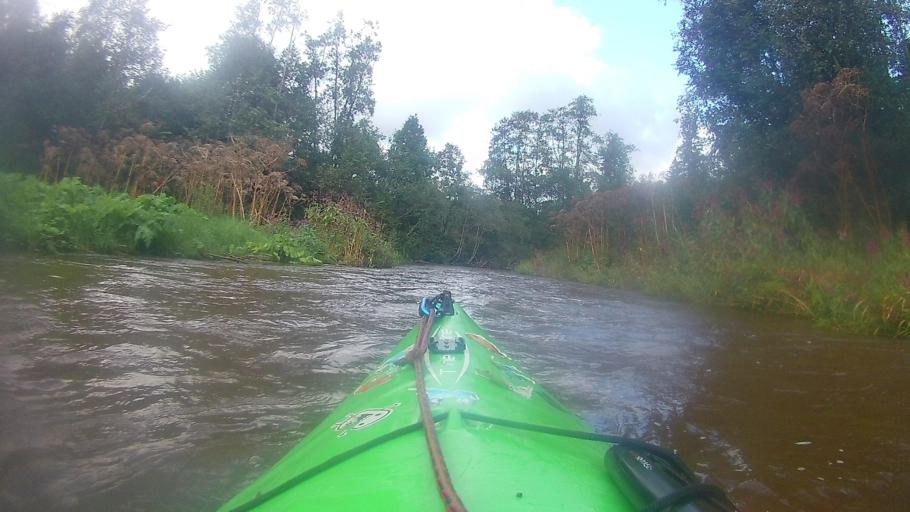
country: LV
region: Talsu Rajons
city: Sabile
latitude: 56.9989
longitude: 22.5967
